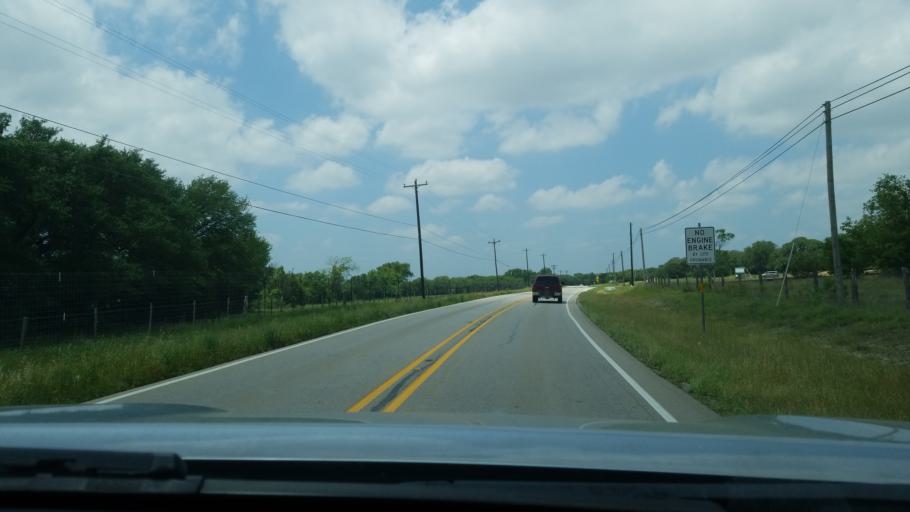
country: US
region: Texas
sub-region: Hays County
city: Dripping Springs
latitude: 30.1602
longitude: -98.0774
